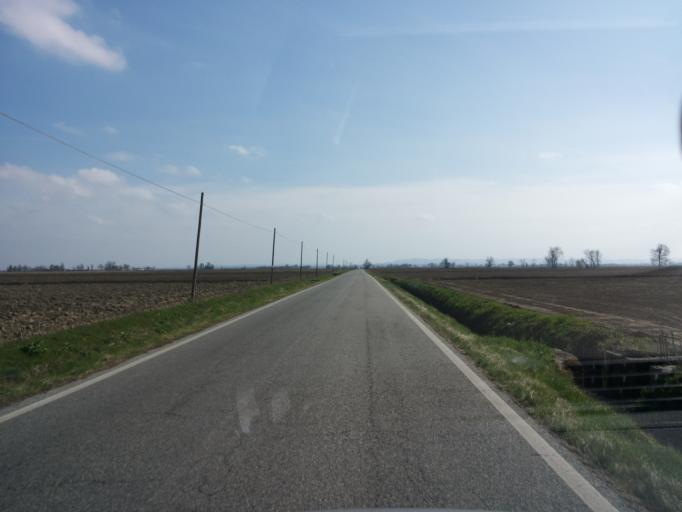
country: IT
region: Piedmont
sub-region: Provincia di Vercelli
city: Crova
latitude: 45.3151
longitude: 8.1989
